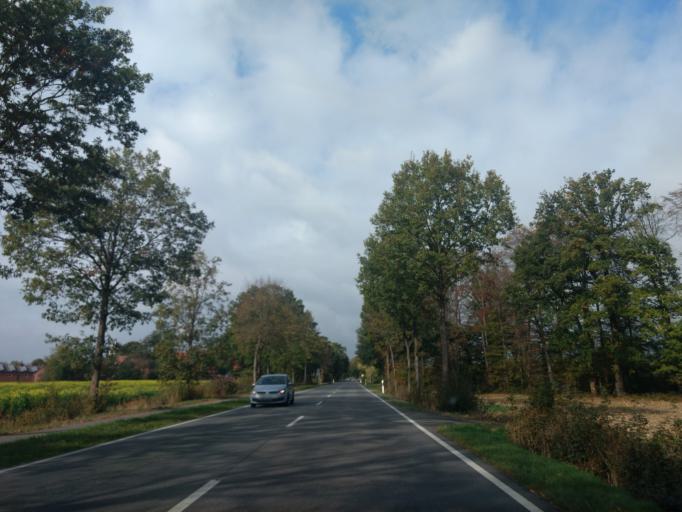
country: DE
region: Lower Saxony
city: Hilter
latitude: 52.1392
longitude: 8.1063
